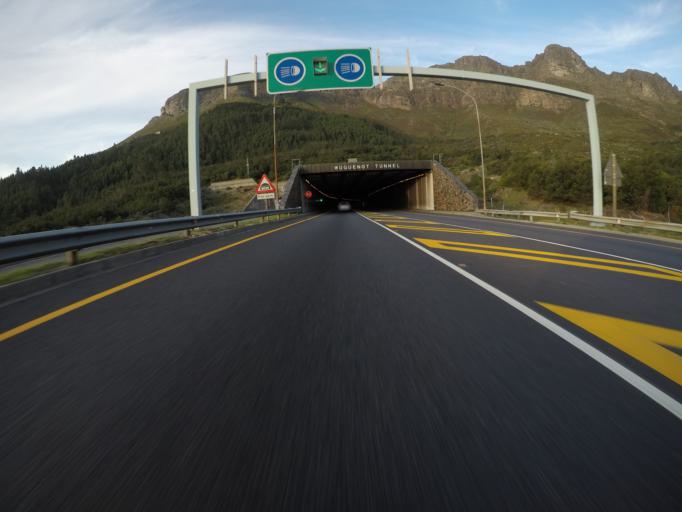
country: ZA
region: Western Cape
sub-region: Cape Winelands District Municipality
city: Paarl
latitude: -33.7351
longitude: 19.0709
